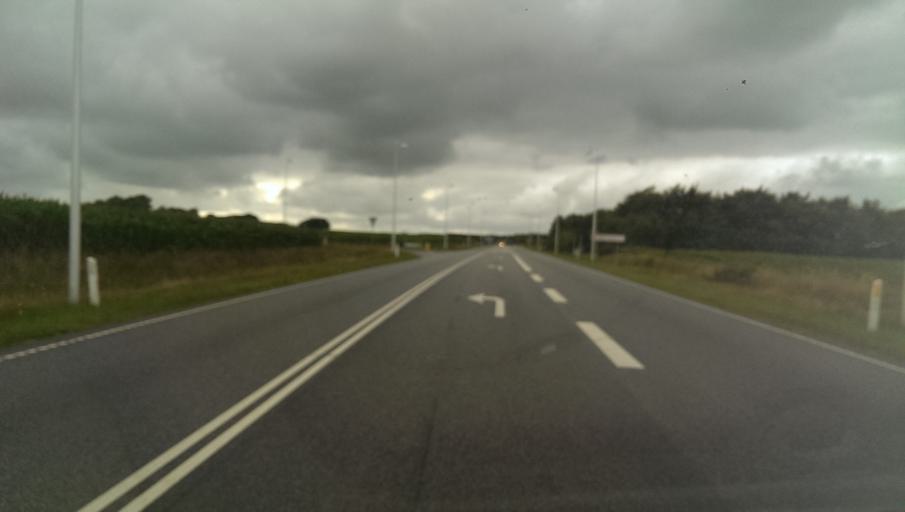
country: DK
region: South Denmark
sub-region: Esbjerg Kommune
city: Tjaereborg
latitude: 55.4946
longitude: 8.6236
